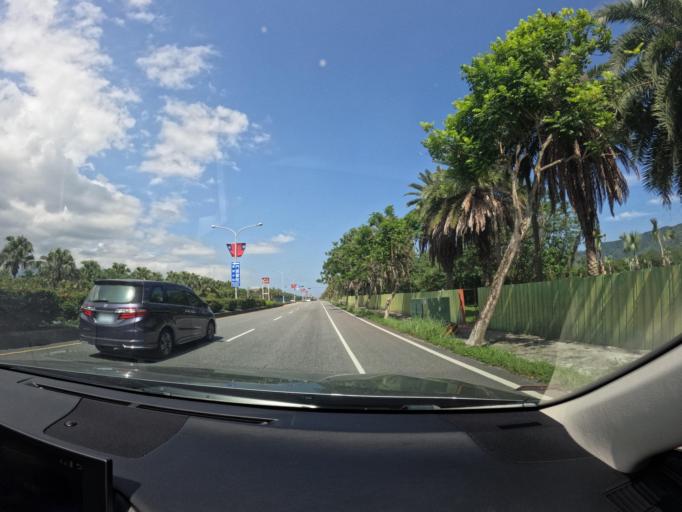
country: TW
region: Taiwan
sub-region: Hualien
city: Hualian
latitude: 23.8626
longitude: 121.5299
